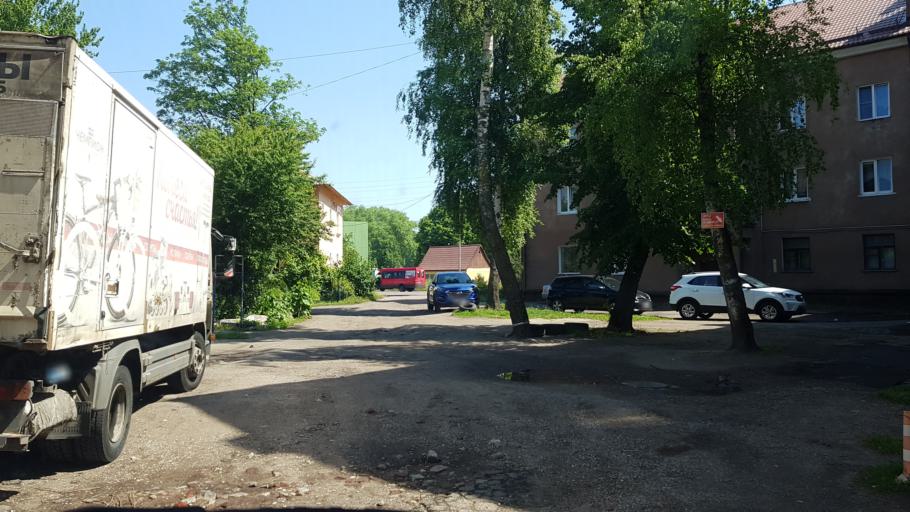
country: RU
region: Kaliningrad
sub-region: Gorod Kaliningrad
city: Baltiysk
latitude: 54.6389
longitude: 19.8922
